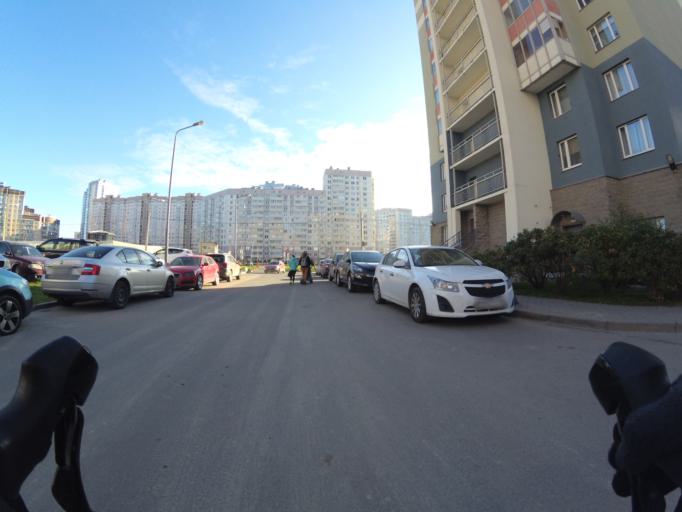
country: RU
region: Leningrad
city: Untolovo
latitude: 59.9976
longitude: 30.2057
